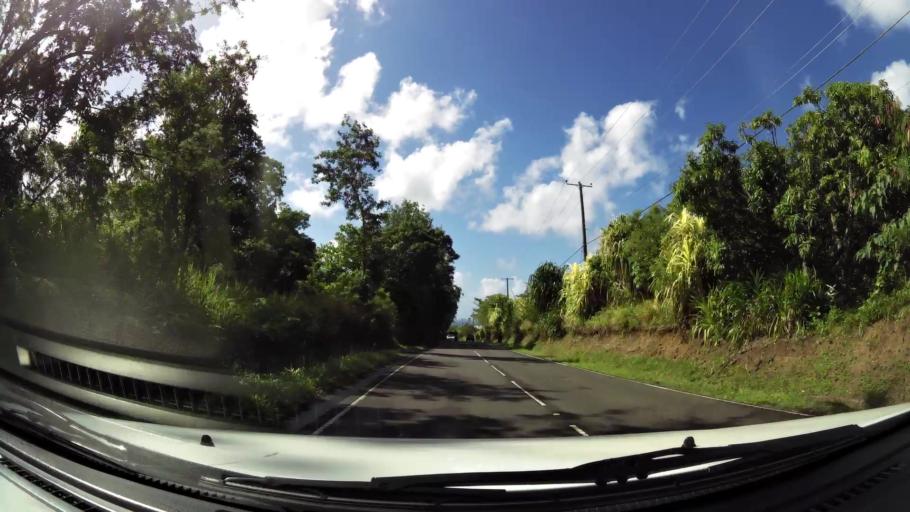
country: LC
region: Choiseul Quarter
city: Choiseul
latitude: 13.7711
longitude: -61.0324
